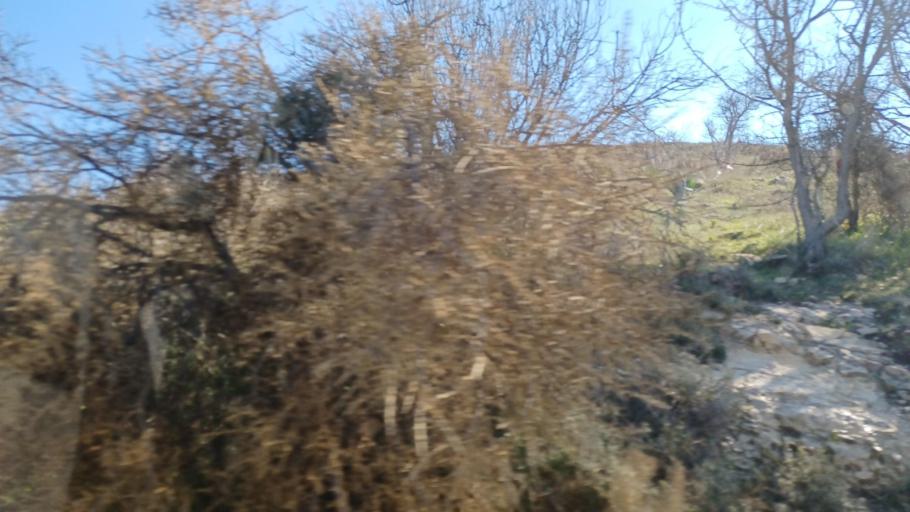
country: CY
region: Limassol
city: Pachna
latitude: 34.8109
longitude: 32.6638
